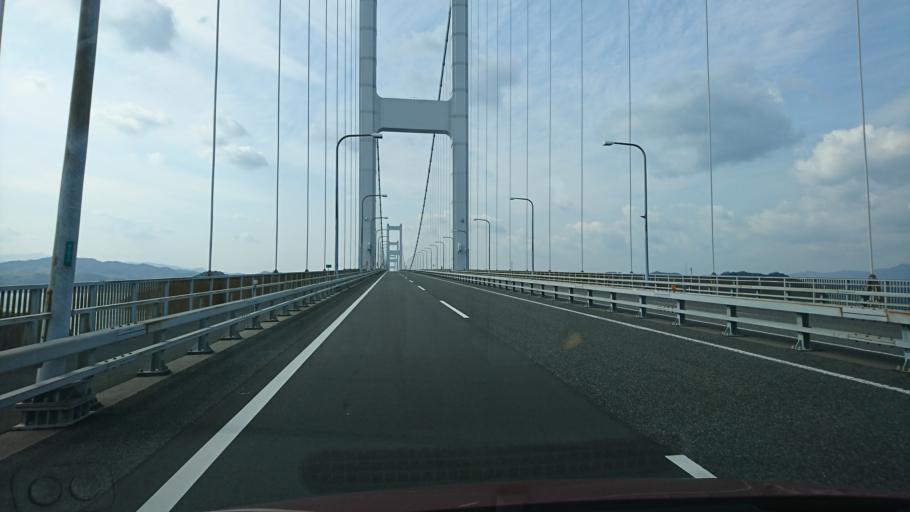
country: JP
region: Hiroshima
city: Takehara
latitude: 34.1236
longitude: 133.0068
